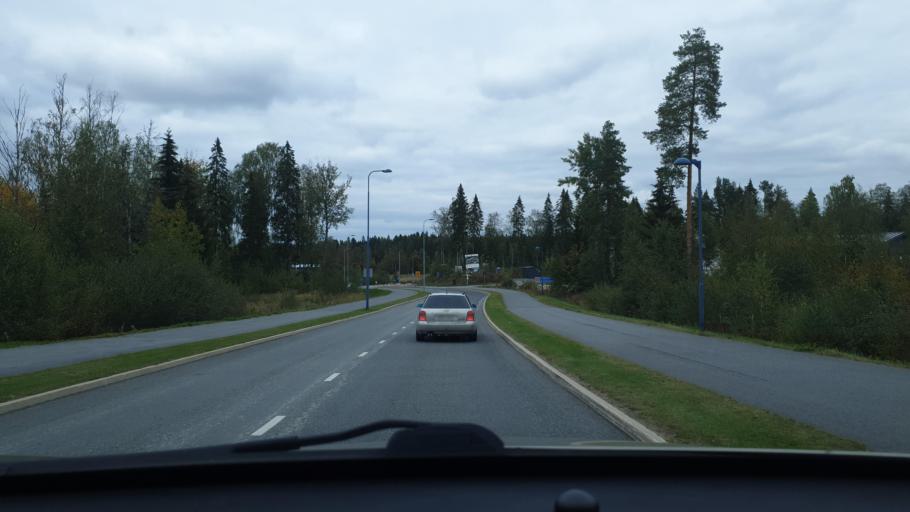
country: FI
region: Ostrobothnia
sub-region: Vaasa
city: Korsholm
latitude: 63.1258
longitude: 21.6644
